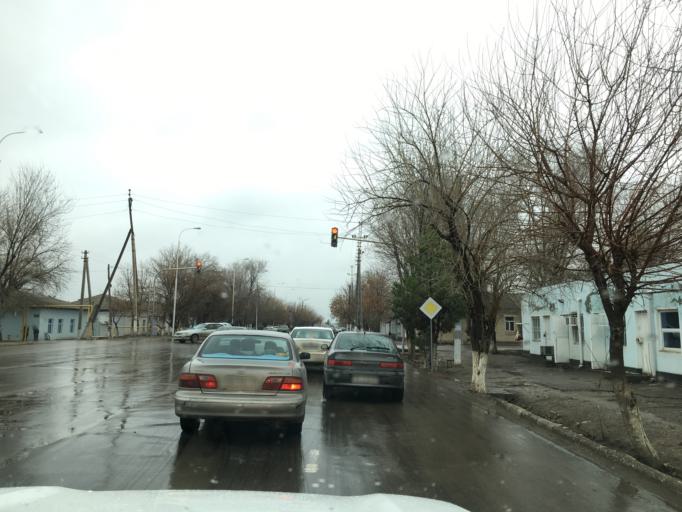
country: TM
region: Mary
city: Yoloeten
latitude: 37.2946
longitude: 62.3621
